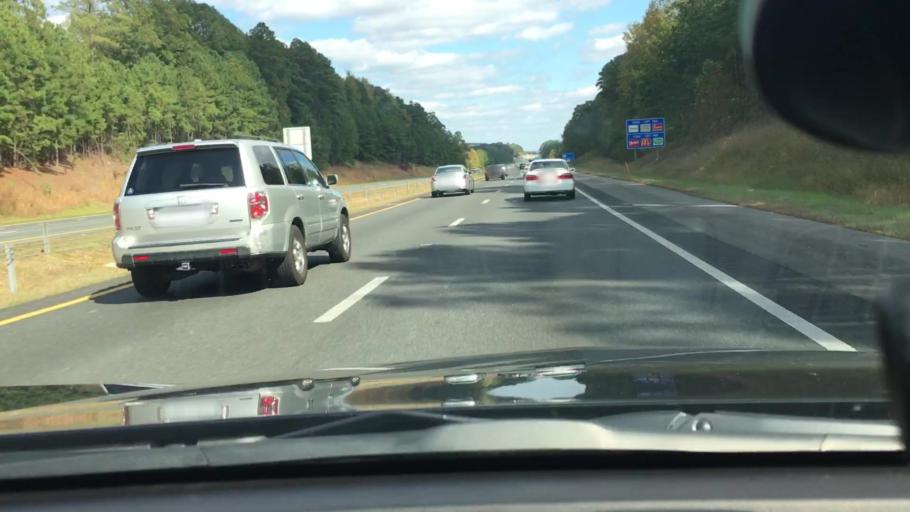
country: US
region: North Carolina
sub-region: Wake County
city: Apex
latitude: 35.7311
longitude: -78.8042
